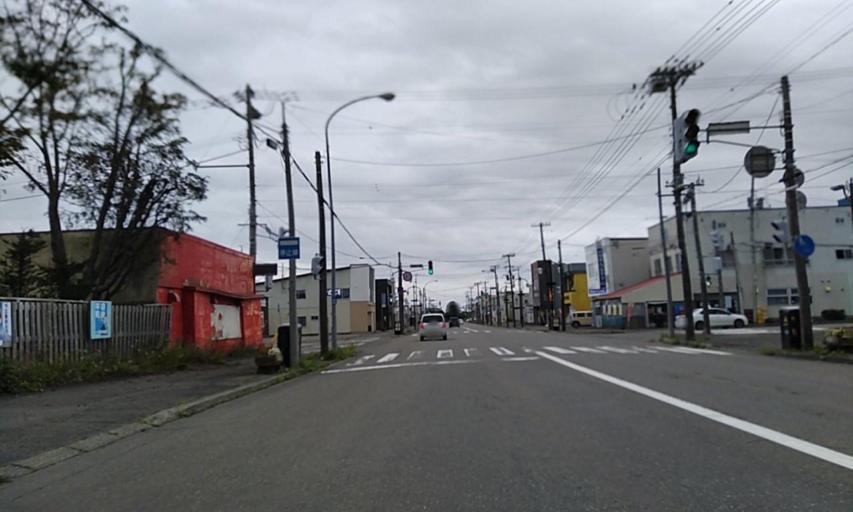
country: JP
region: Hokkaido
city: Obihiro
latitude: 42.2878
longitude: 143.3163
